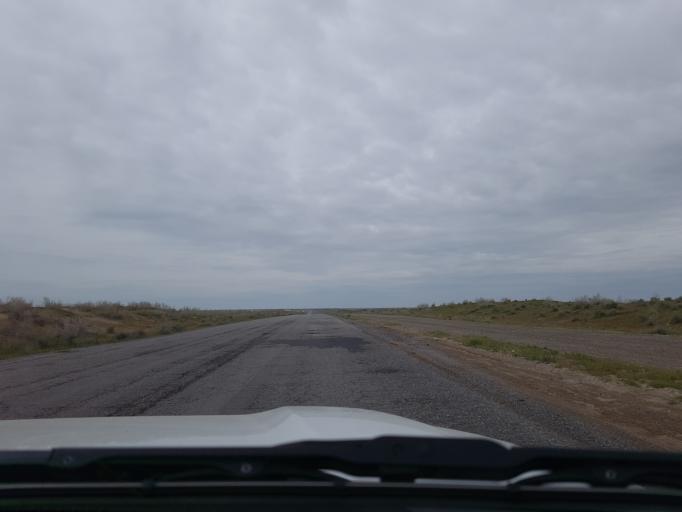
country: TM
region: Mary
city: Bayramaly
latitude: 38.1113
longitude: 62.8140
